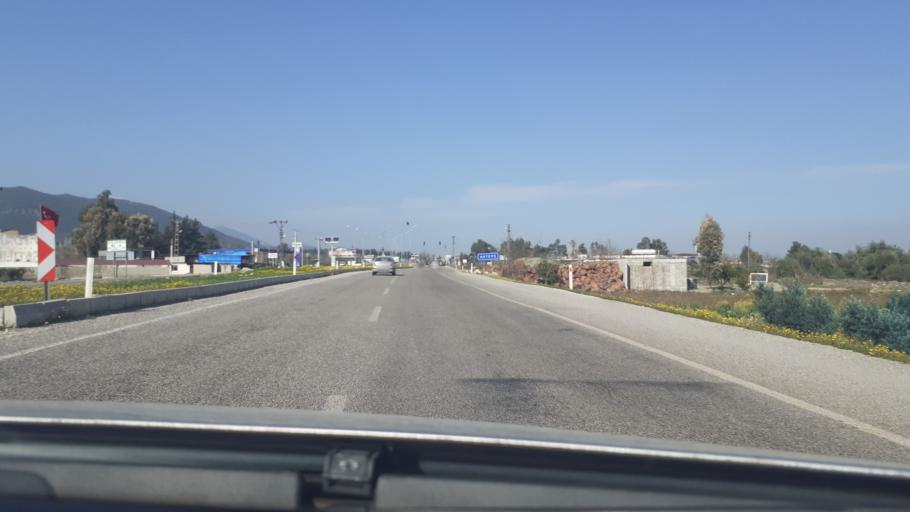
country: TR
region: Hatay
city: Aktepe
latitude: 36.6905
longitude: 36.4735
